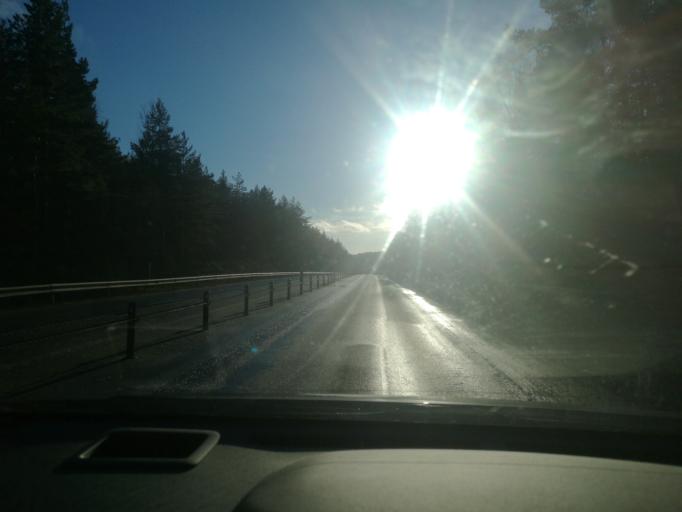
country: SE
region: OEstergoetland
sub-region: Norrkopings Kommun
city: Jursla
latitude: 58.7095
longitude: 16.1601
